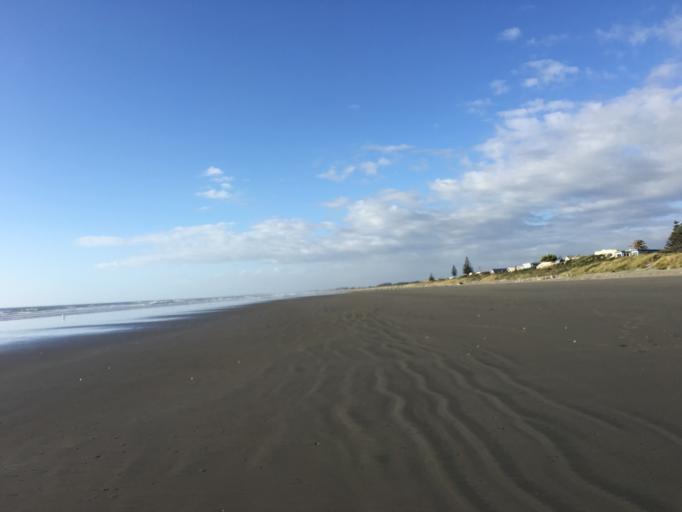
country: NZ
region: Wellington
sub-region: Kapiti Coast District
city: Paraparaumu
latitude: -40.8559
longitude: 175.0291
